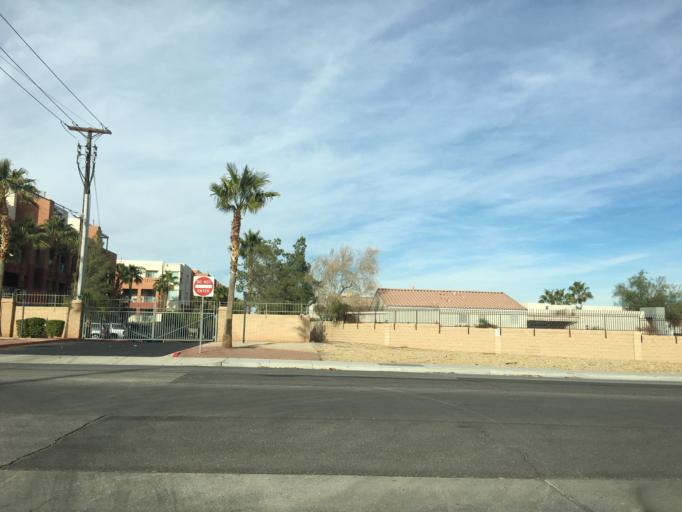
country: US
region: Nevada
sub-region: Clark County
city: Enterprise
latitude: 36.0205
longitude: -115.1681
